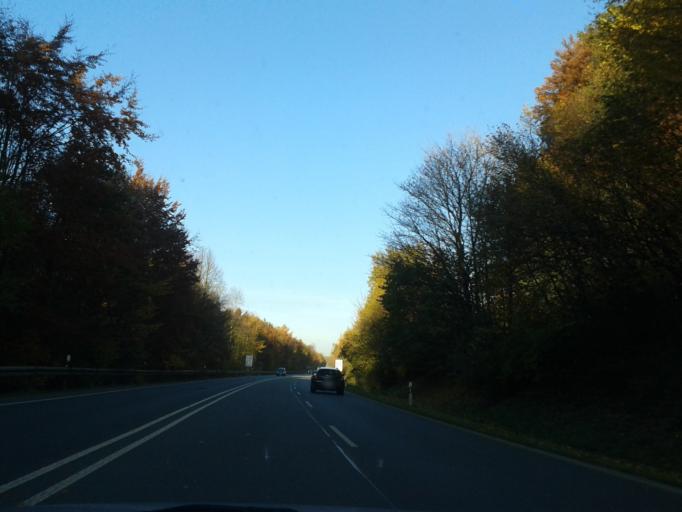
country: DE
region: North Rhine-Westphalia
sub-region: Regierungsbezirk Arnsberg
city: Ruthen
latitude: 51.4951
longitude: 8.4478
